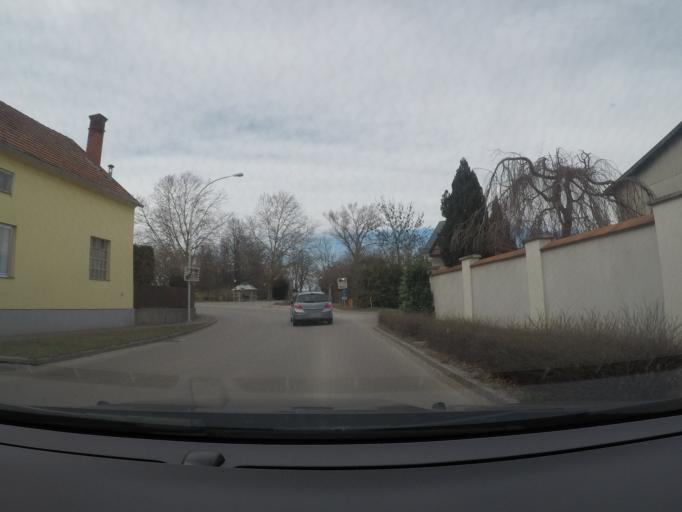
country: AT
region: Lower Austria
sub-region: Politischer Bezirk Neunkirchen
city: Pitten
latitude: 47.7280
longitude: 16.1711
